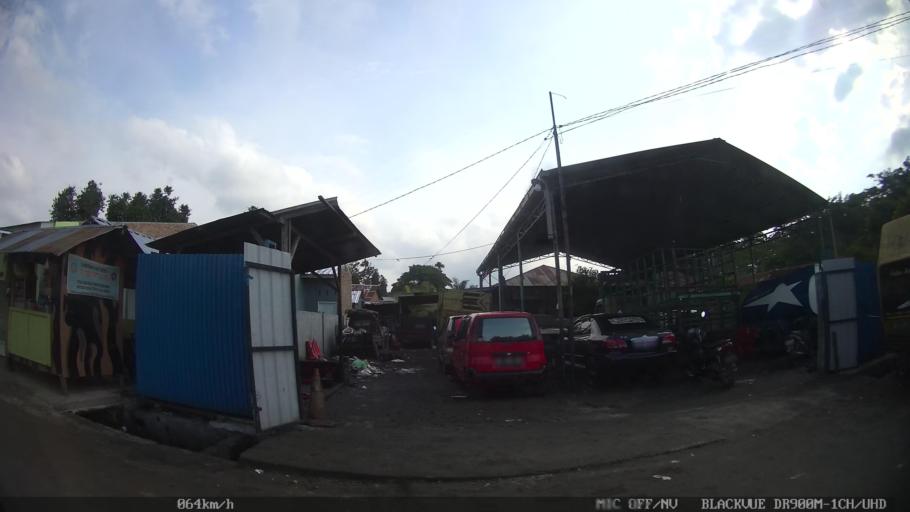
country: ID
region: North Sumatra
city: Percut
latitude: 3.5648
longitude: 98.7915
